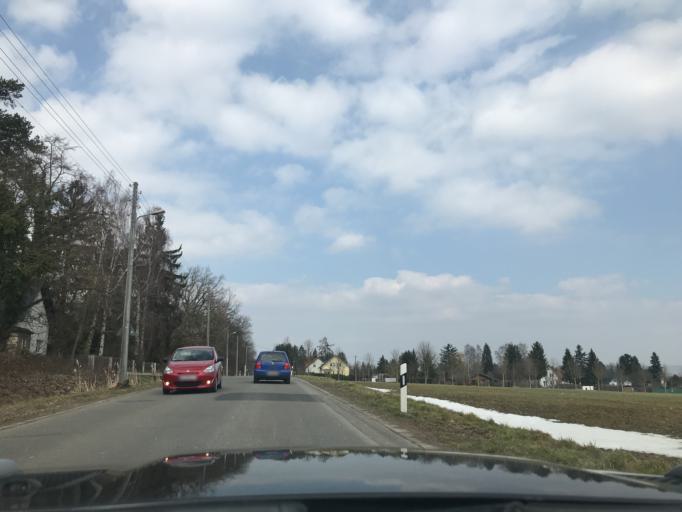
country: DE
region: Thuringia
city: Oberdorla
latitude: 51.1983
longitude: 10.3968
